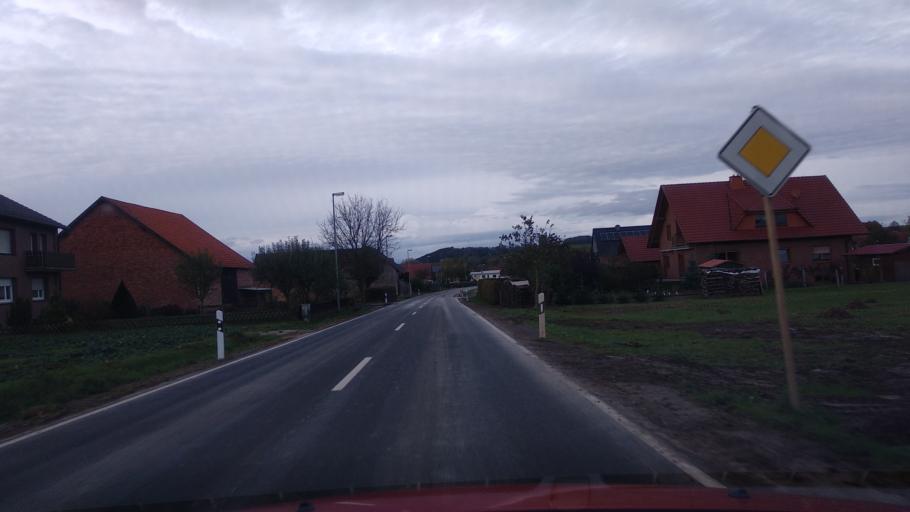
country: DE
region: North Rhine-Westphalia
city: Brakel
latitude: 51.6843
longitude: 9.2260
